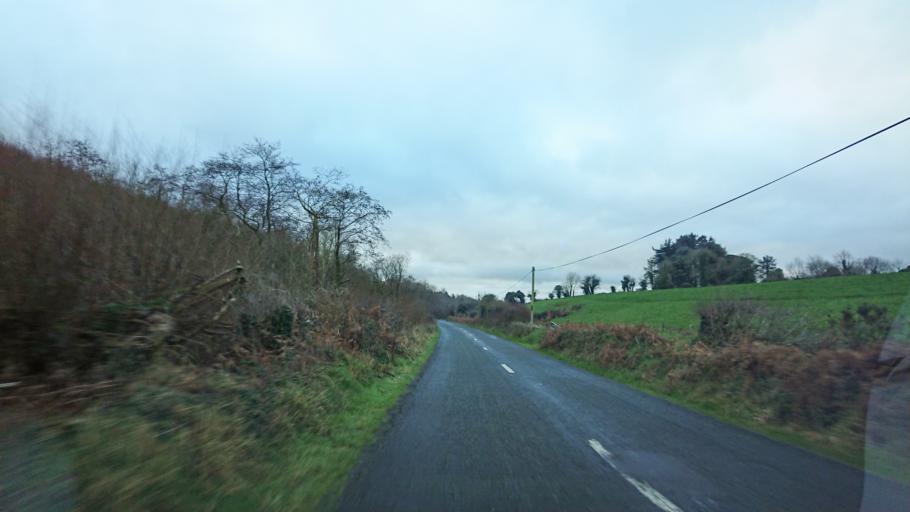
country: IE
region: Munster
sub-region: Waterford
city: Portlaw
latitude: 52.2200
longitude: -7.4147
